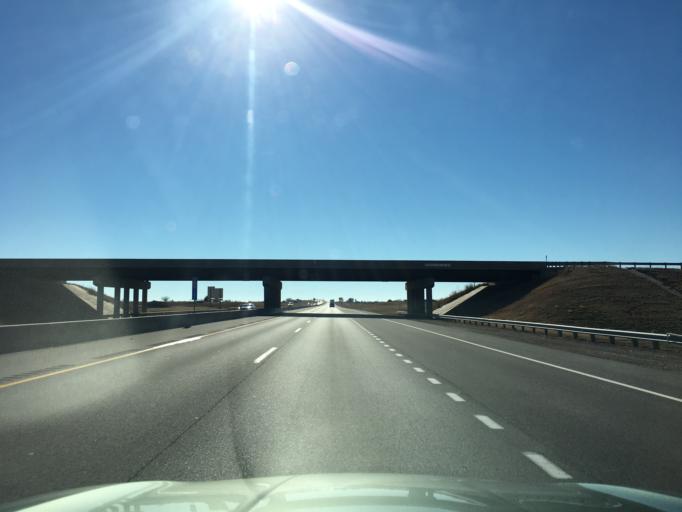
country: US
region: Kansas
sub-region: Sumner County
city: Wellington
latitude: 37.2770
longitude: -97.3404
